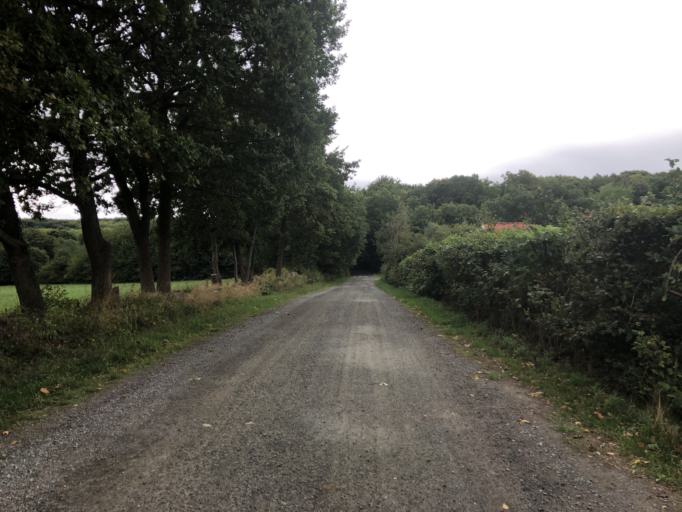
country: SE
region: Skane
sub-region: Simrishamns Kommun
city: Kivik
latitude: 55.6419
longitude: 14.2594
